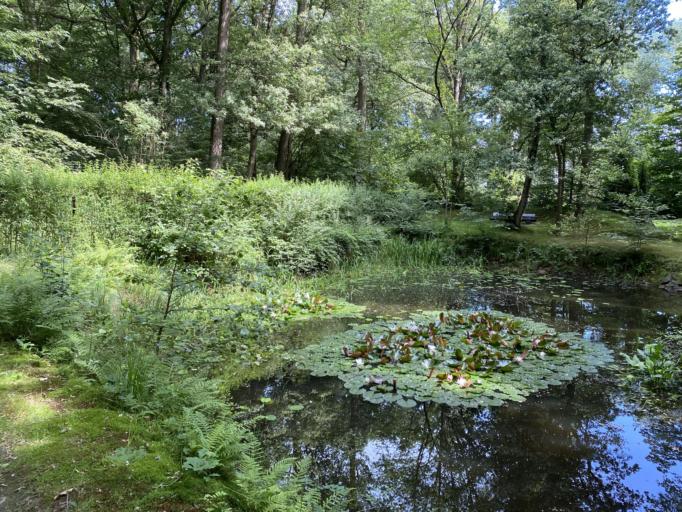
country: NL
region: Limburg
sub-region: Gemeente Roerdalen
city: Posterholt
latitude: 51.1034
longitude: 6.0533
